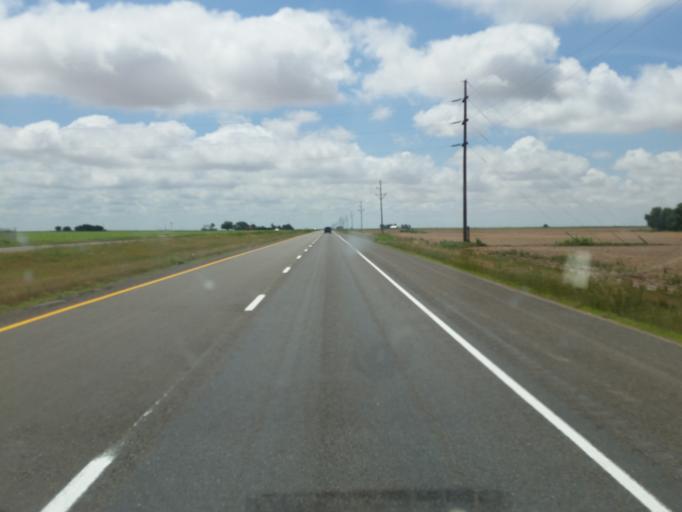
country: US
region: Texas
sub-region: Lubbock County
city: Slaton
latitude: 33.4033
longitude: -101.6175
